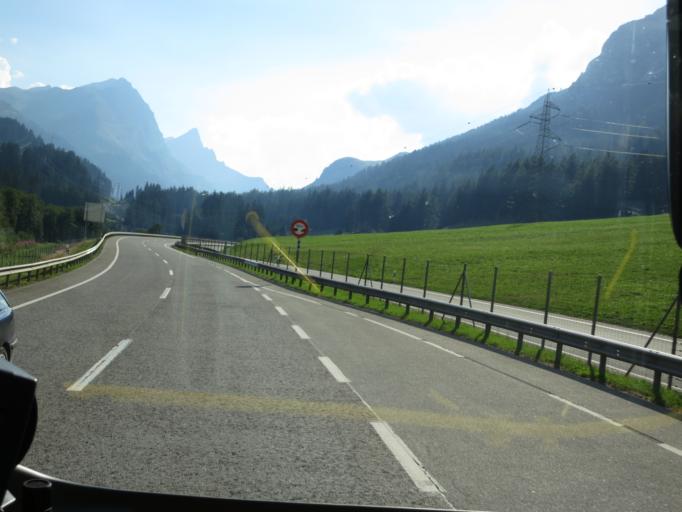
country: CH
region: Grisons
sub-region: Hinterrhein District
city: Thusis
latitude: 46.5671
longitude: 9.3602
